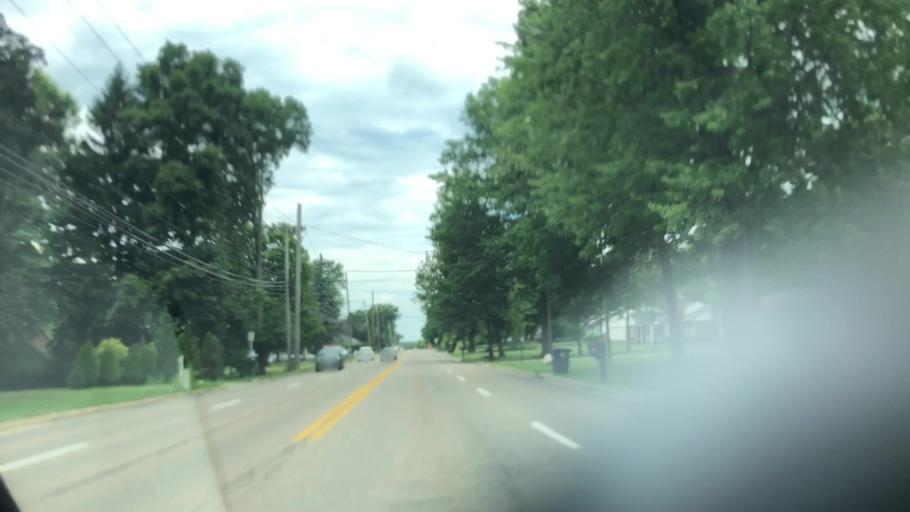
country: US
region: Ohio
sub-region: Summit County
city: Fairlawn
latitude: 41.1207
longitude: -81.6098
